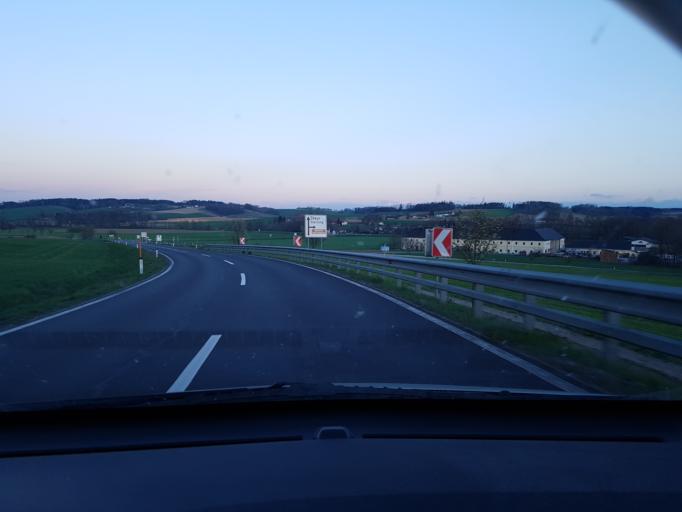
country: AT
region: Upper Austria
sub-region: Politischer Bezirk Linz-Land
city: Sankt Florian
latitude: 48.2018
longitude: 14.3572
